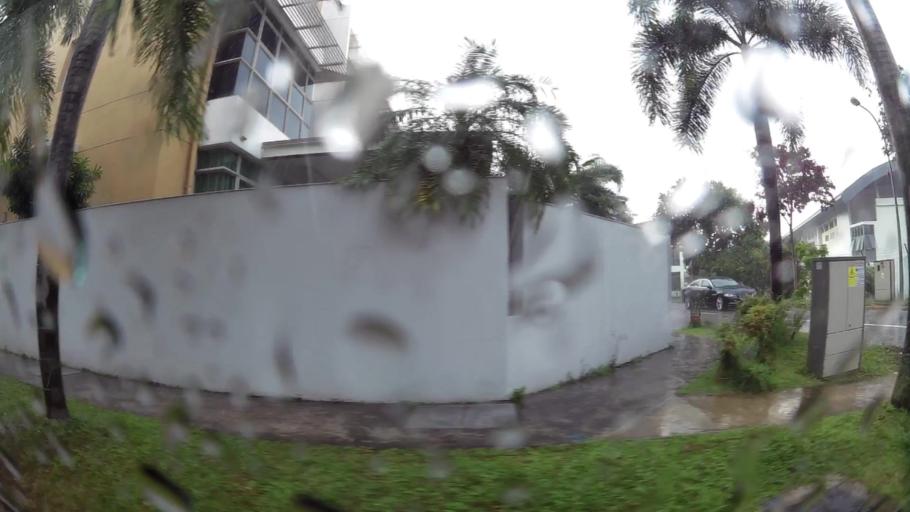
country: SG
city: Singapore
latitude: 1.3395
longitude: 103.9539
